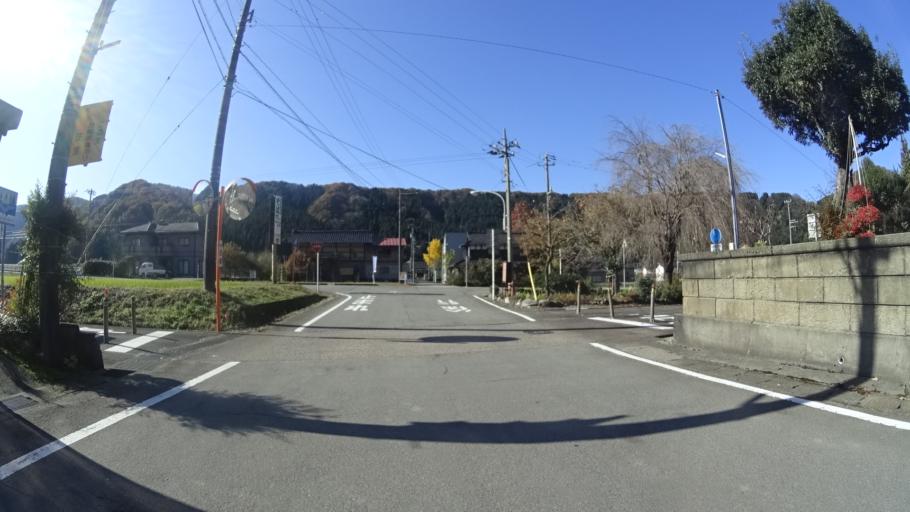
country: JP
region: Ishikawa
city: Tsurugi-asahimachi
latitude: 36.3435
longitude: 136.6304
